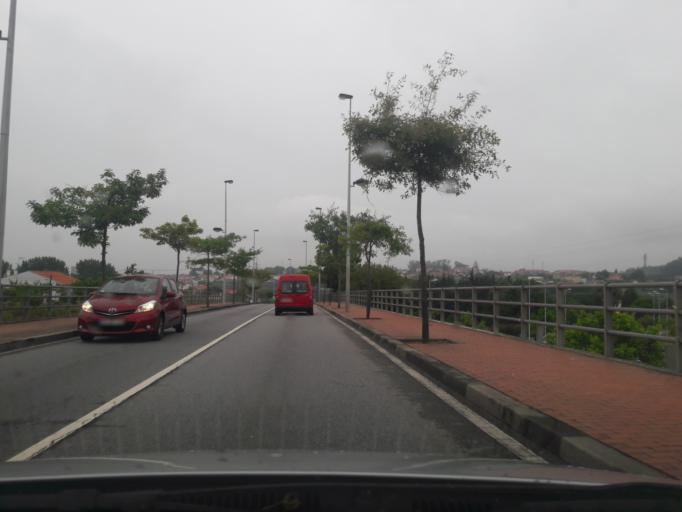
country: PT
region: Porto
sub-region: Vila do Conde
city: Arvore
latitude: 41.3333
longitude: -8.7211
